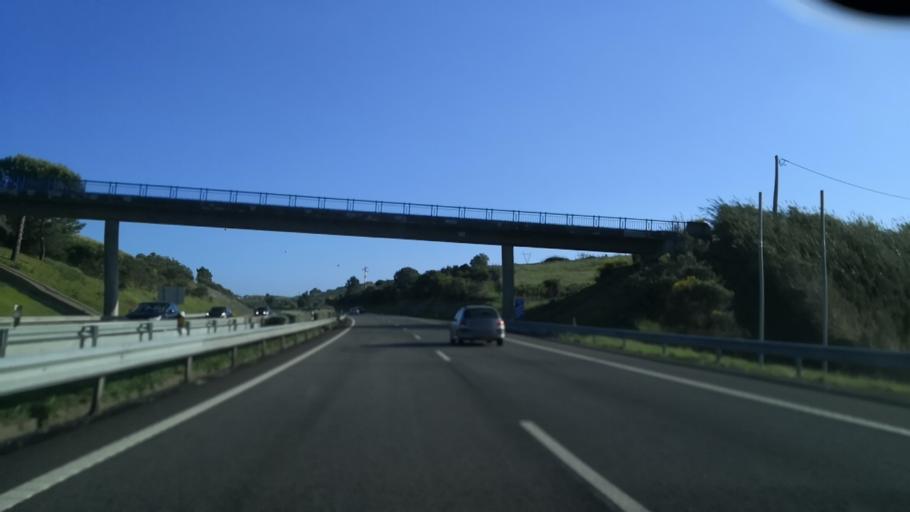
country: PT
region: Lisbon
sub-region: Mafra
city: Milharado
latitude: 38.9977
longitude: -9.2161
